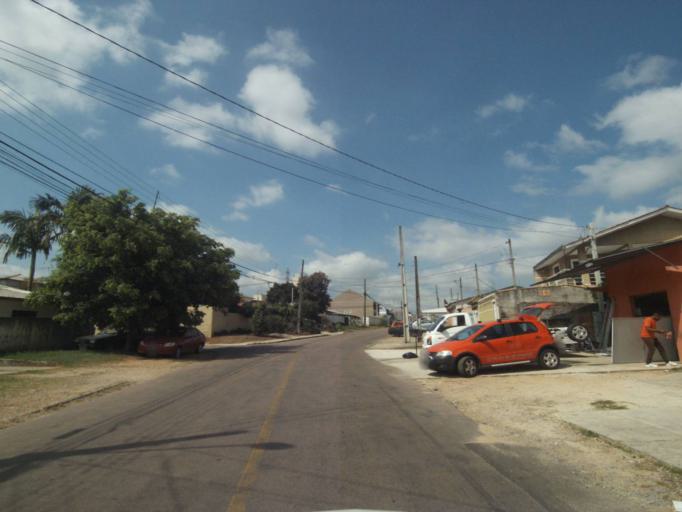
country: BR
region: Parana
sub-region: Sao Jose Dos Pinhais
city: Sao Jose dos Pinhais
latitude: -25.5410
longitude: -49.2690
